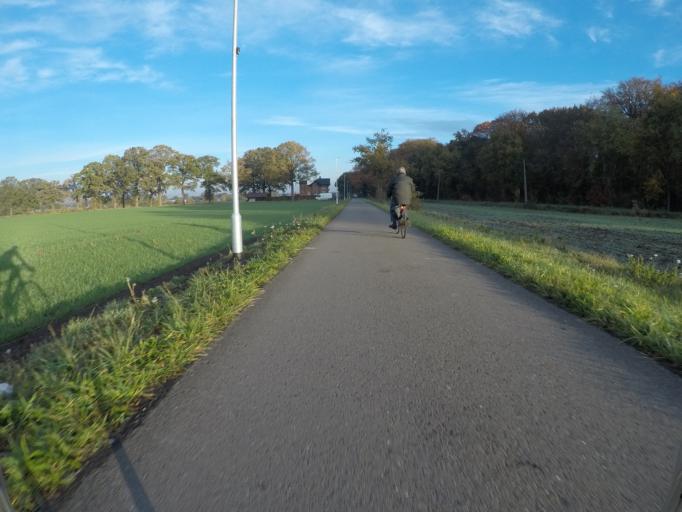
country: BE
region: Flanders
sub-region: Provincie Antwerpen
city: Herentals
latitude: 51.1406
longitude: 4.8226
